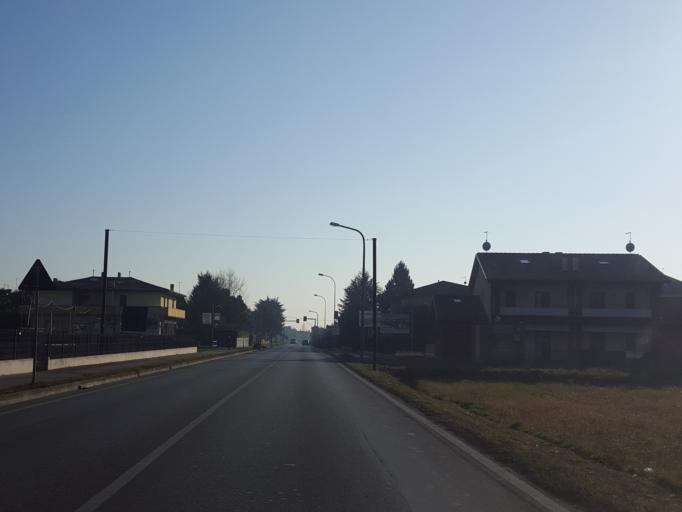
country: IT
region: Veneto
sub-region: Provincia di Vicenza
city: Marola
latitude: 45.5347
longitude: 11.6301
